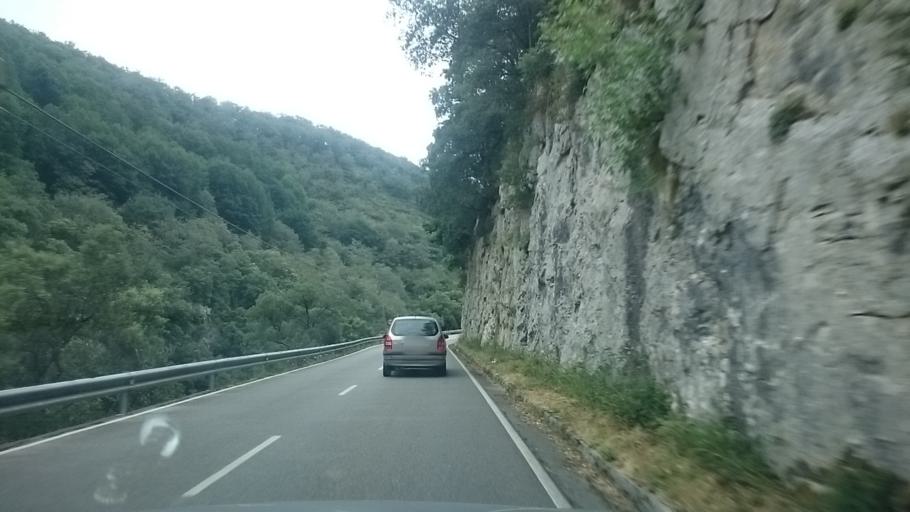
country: ES
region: Asturias
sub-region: Province of Asturias
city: Carrena
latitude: 43.2895
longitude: -4.8289
